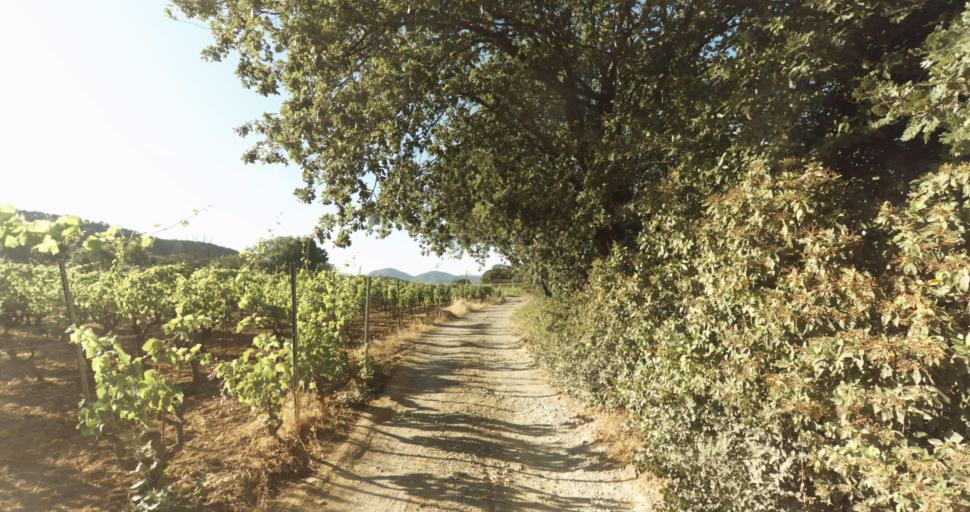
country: FR
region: Provence-Alpes-Cote d'Azur
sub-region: Departement du Var
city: Gassin
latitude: 43.2321
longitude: 6.5926
